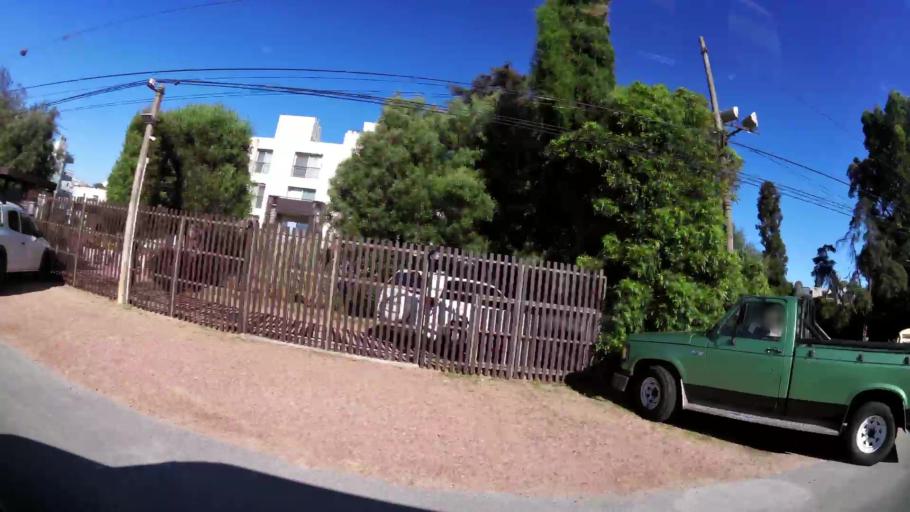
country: UY
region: Canelones
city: Barra de Carrasco
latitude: -34.8677
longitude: -56.0311
